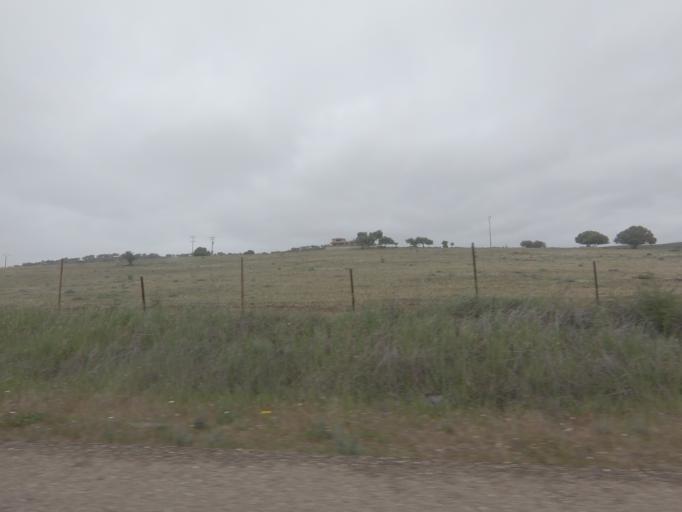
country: ES
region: Extremadura
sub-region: Provincia de Badajoz
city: La Roca de la Sierra
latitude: 39.1084
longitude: -6.7057
